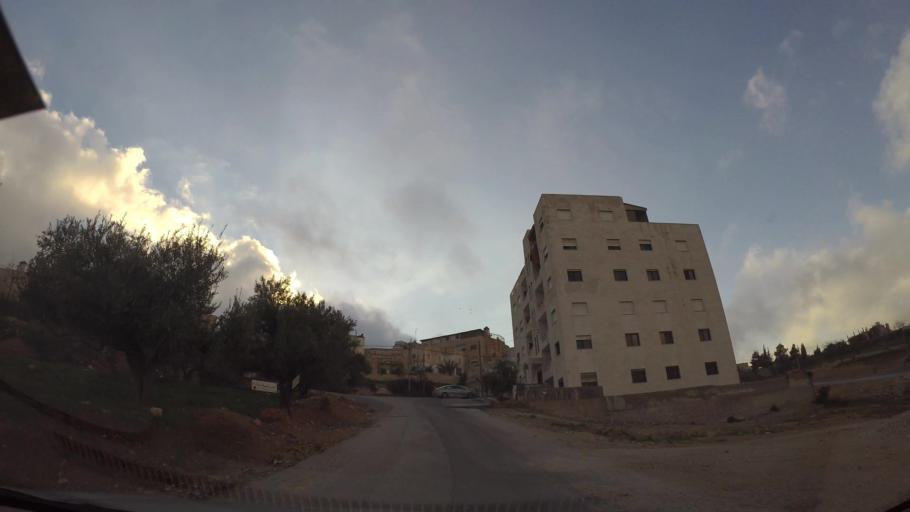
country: JO
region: Amman
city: Al Jubayhah
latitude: 32.0505
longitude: 35.8889
